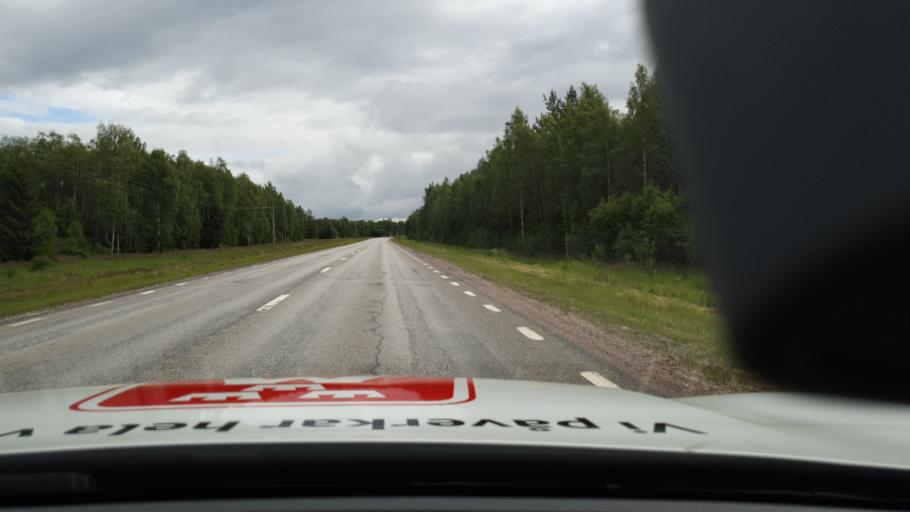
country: SE
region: Norrbotten
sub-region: Pitea Kommun
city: Rosvik
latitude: 65.5764
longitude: 21.7233
